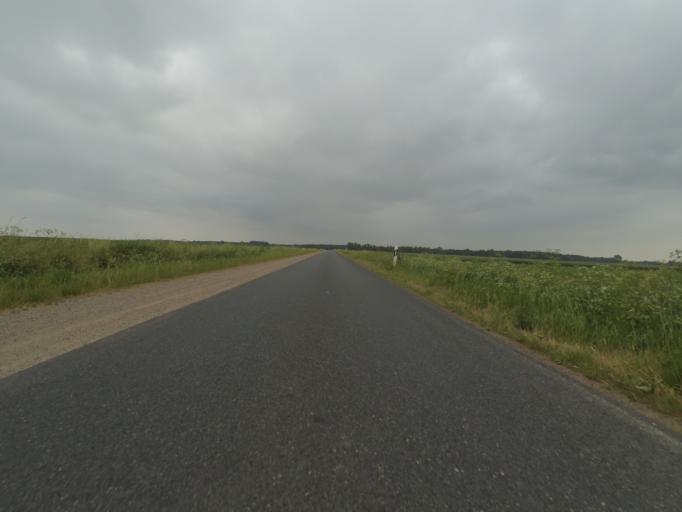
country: DE
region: Mecklenburg-Vorpommern
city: Spornitz
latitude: 53.3632
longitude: 11.6821
